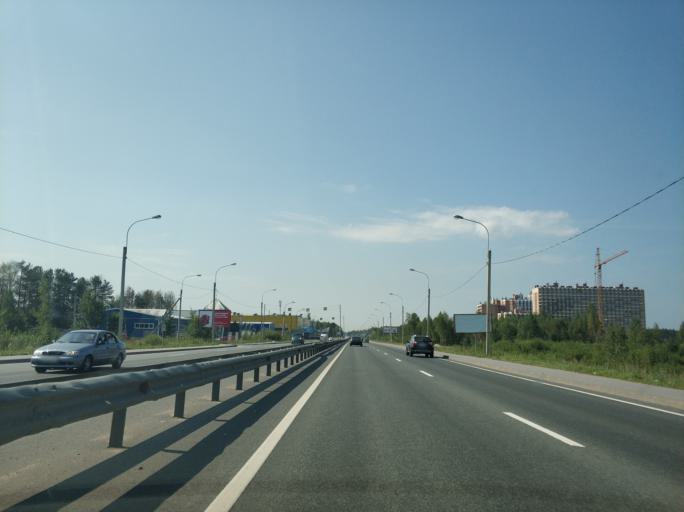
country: RU
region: Leningrad
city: Vsevolozhsk
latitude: 60.0242
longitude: 30.6099
